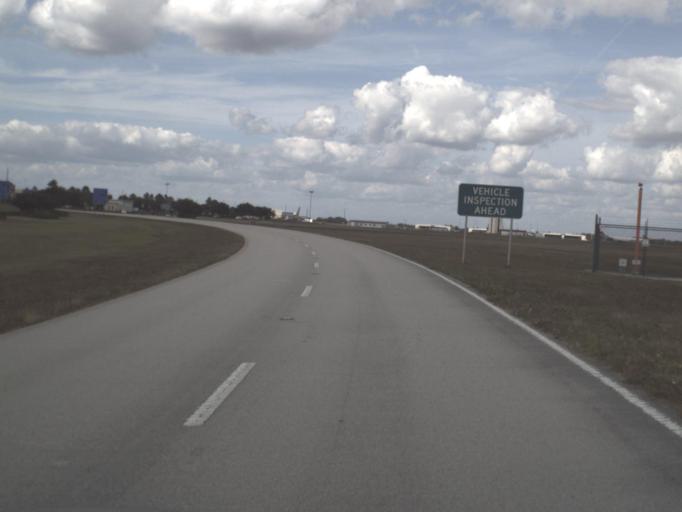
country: US
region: Florida
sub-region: Seminole County
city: Midway
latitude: 28.7695
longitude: -81.2376
